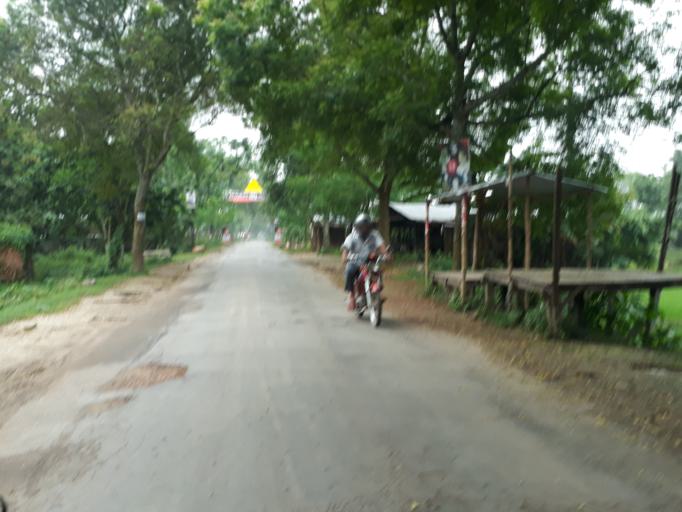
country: BD
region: Khulna
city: Kaliganj
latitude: 23.3506
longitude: 88.9245
